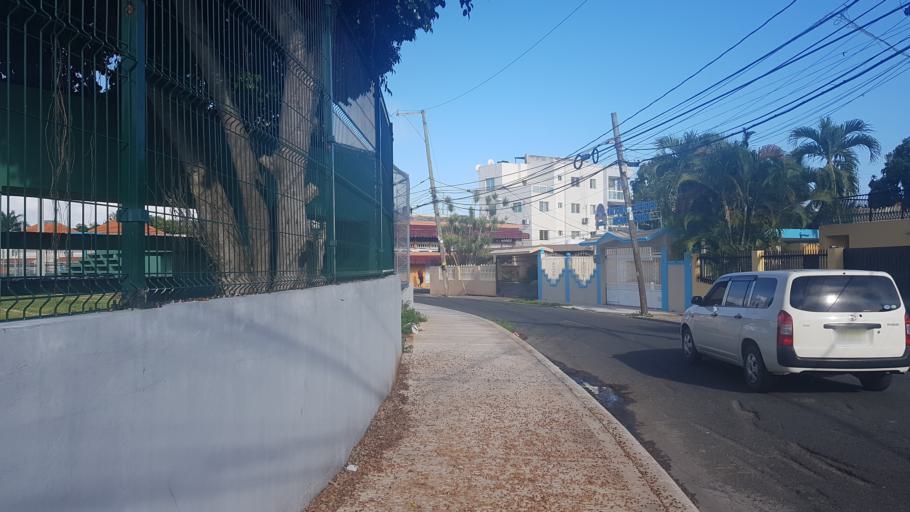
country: DO
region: Santo Domingo
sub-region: Santo Domingo
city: Santo Domingo Este
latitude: 18.4868
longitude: -69.8474
